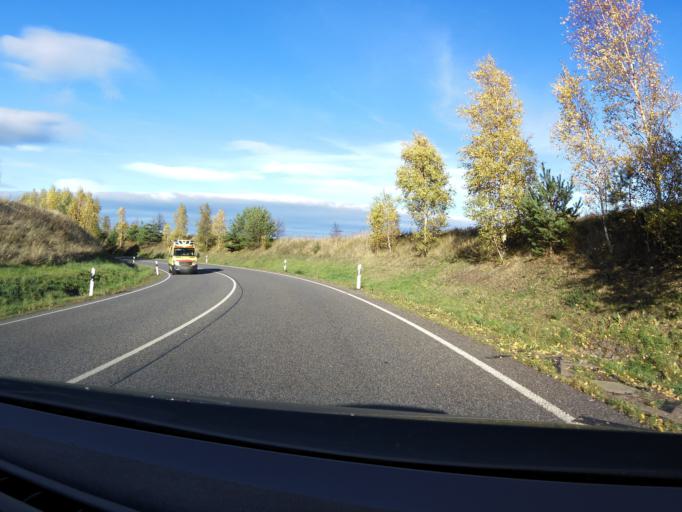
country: DE
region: Thuringia
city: Geraberg
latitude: 50.7223
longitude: 10.8375
